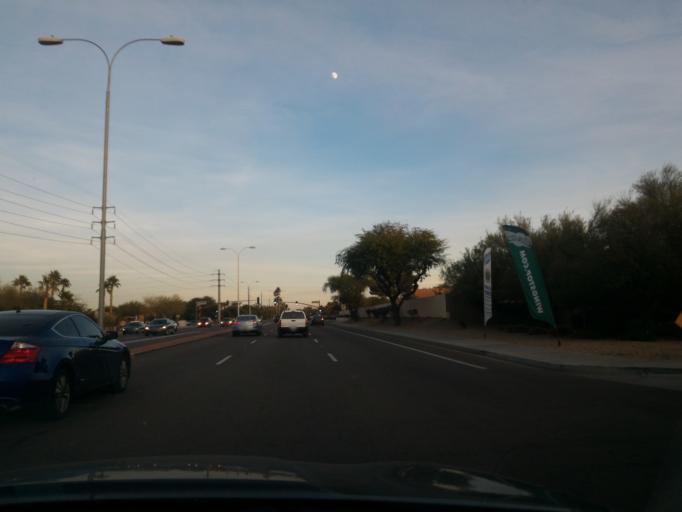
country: US
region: Arizona
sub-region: Maricopa County
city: Guadalupe
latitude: 33.3053
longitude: -111.9435
